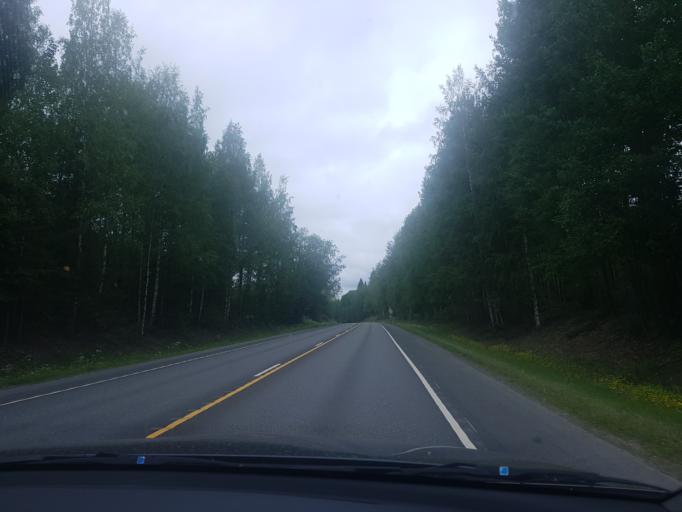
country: FI
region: Pirkanmaa
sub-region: Tampere
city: Paelkaene
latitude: 61.3955
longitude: 24.2112
